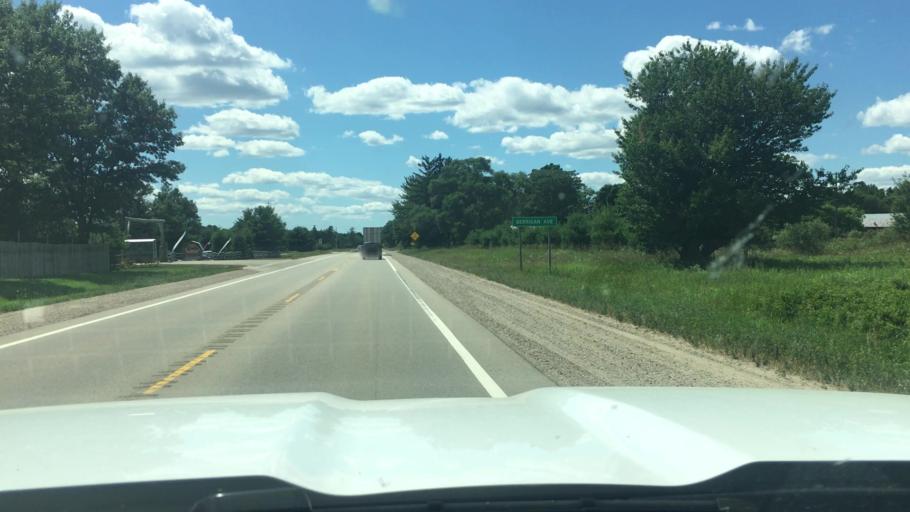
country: US
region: Michigan
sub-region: Kent County
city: Cedar Springs
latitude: 43.1759
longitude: -85.4780
